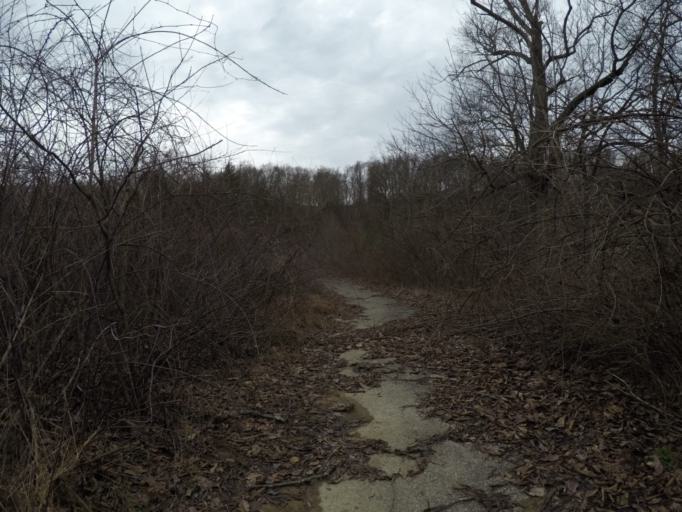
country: US
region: Ohio
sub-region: Lawrence County
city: Burlington
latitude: 38.3822
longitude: -82.5093
